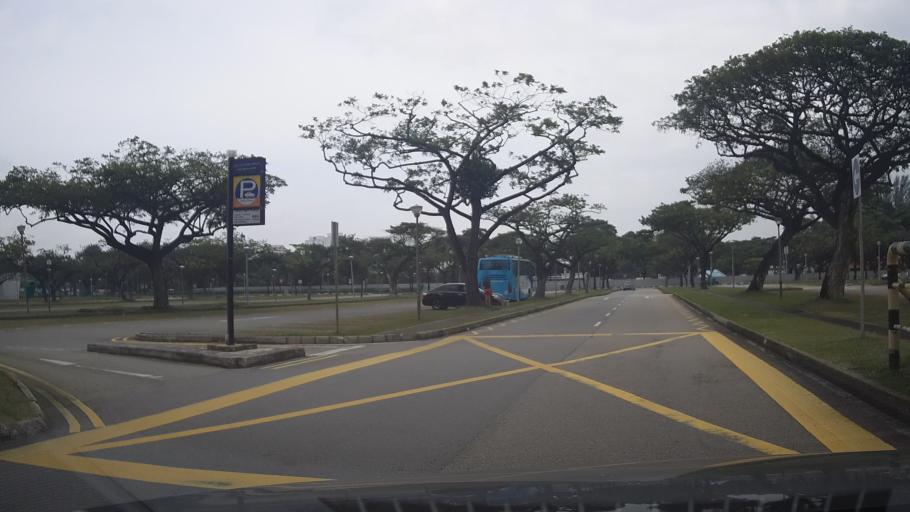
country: SG
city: Singapore
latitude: 1.3021
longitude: 103.8771
